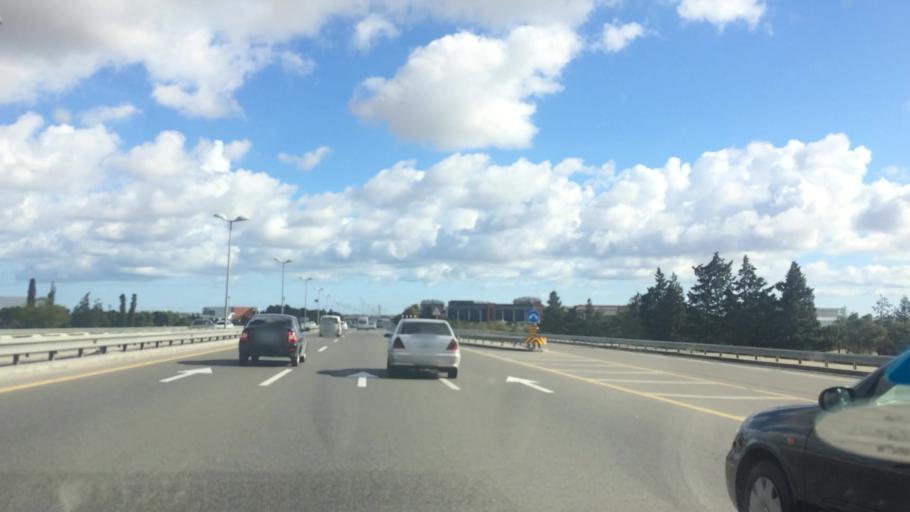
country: AZ
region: Baki
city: Biny Selo
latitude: 40.4517
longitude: 50.0617
